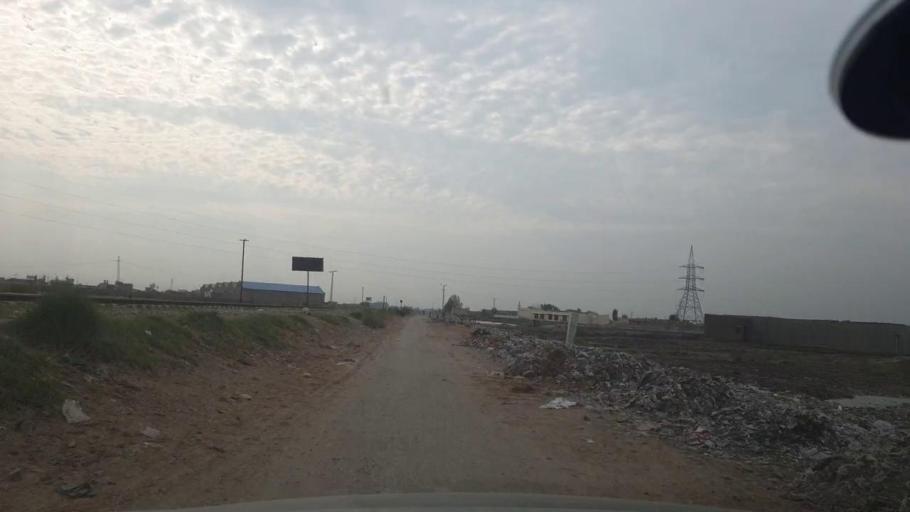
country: PK
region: Sindh
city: Jacobabad
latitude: 28.2611
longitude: 68.4494
